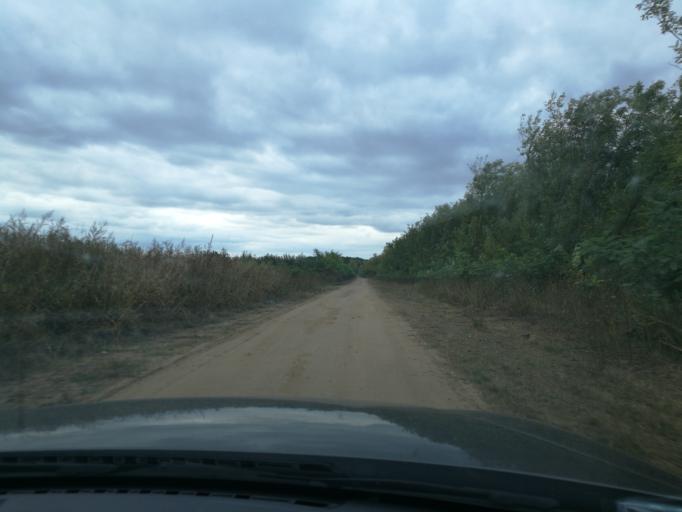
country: HU
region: Szabolcs-Szatmar-Bereg
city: Nyirpazony
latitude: 47.9913
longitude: 21.7885
